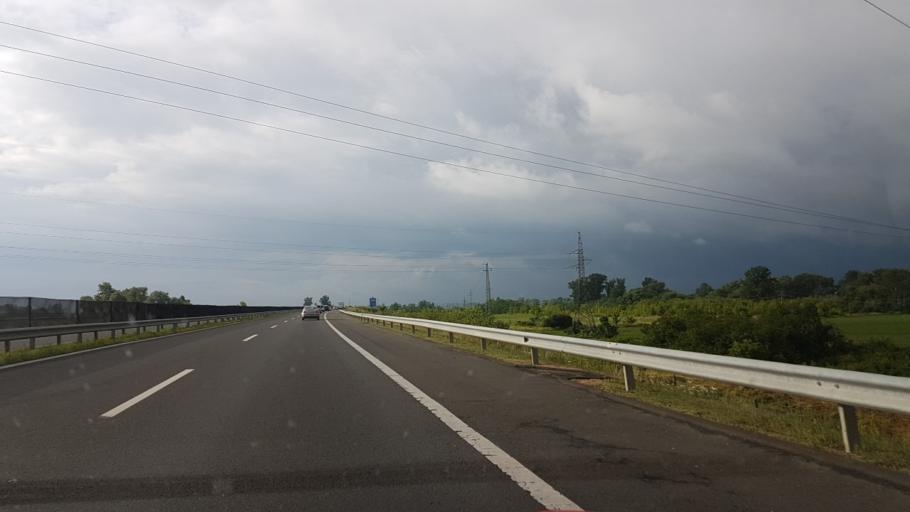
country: HU
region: Borsod-Abauj-Zemplen
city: Felsozsolca
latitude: 48.0947
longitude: 20.8484
